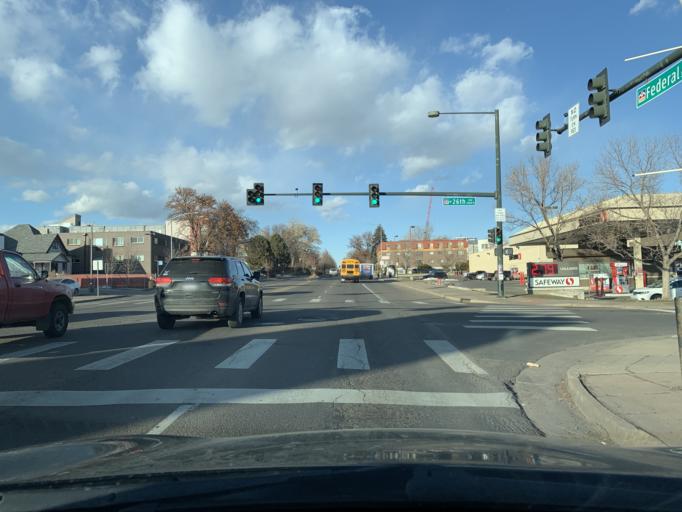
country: US
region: Colorado
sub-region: Jefferson County
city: Edgewater
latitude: 39.7547
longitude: -105.0252
